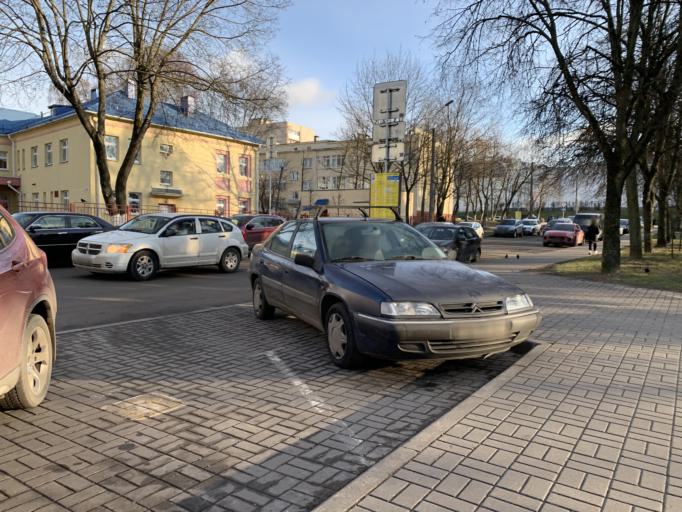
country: BY
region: Minsk
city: Minsk
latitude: 53.9143
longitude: 27.5859
